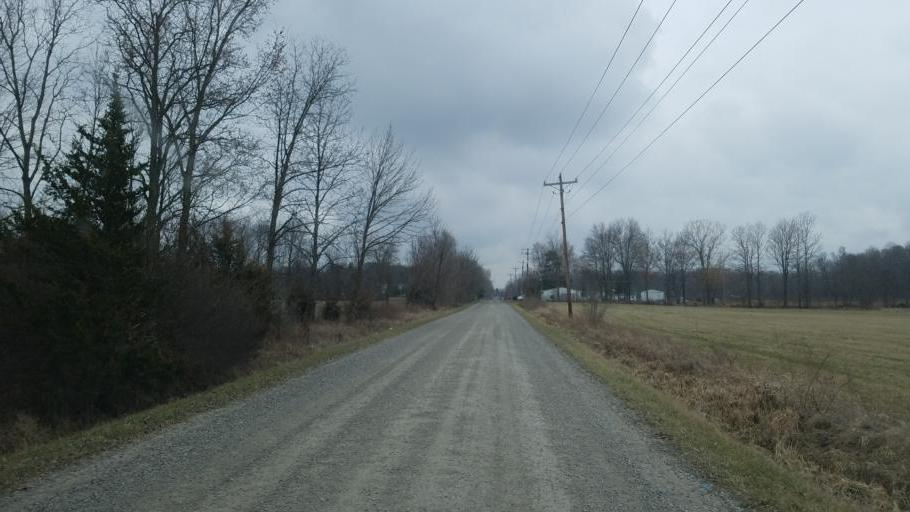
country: US
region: Ohio
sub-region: Morrow County
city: Cardington
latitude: 40.4071
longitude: -82.8520
